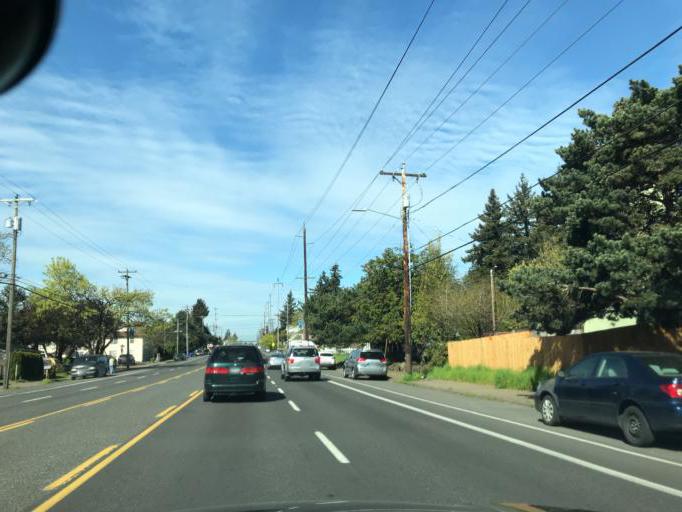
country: US
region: Oregon
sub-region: Multnomah County
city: Lents
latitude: 45.5041
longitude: -122.5172
